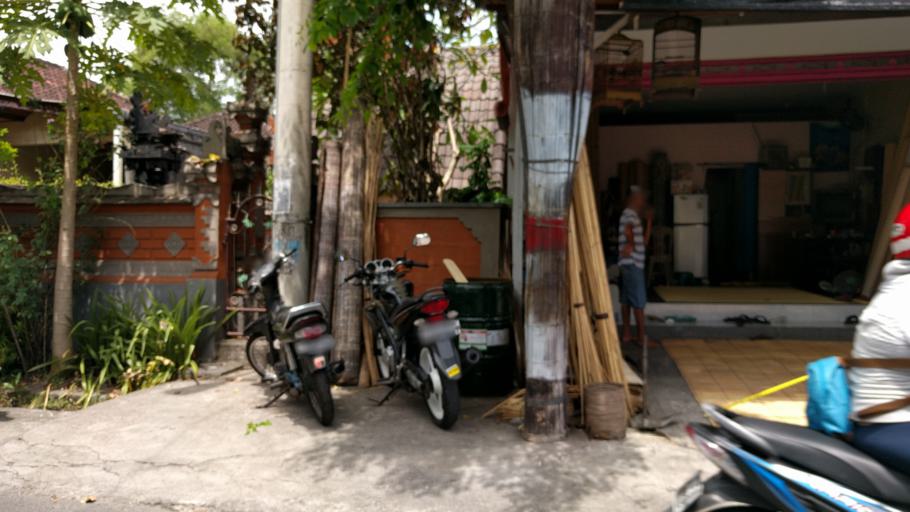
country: ID
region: Bali
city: Banjar Gunungpande
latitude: -8.6556
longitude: 115.1477
